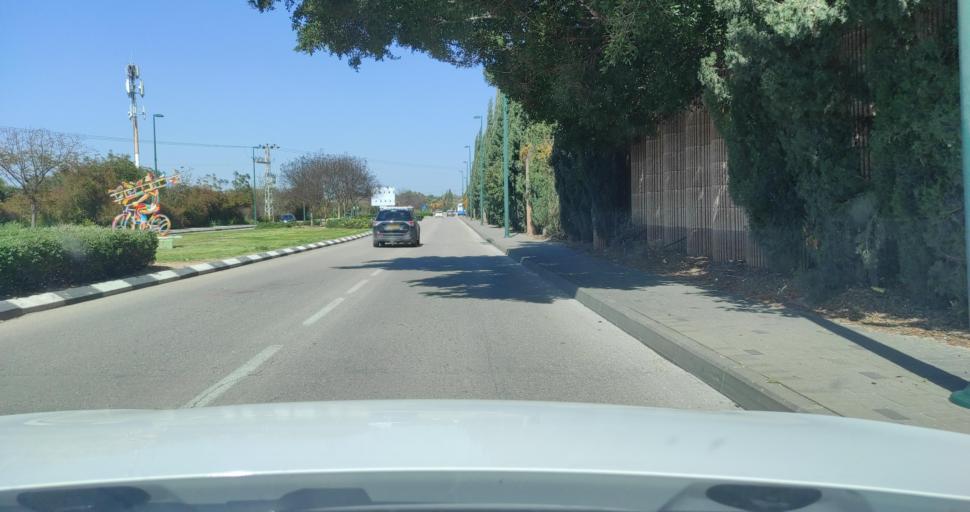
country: IL
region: Central District
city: Bet Yizhaq
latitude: 32.3155
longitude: 34.8799
